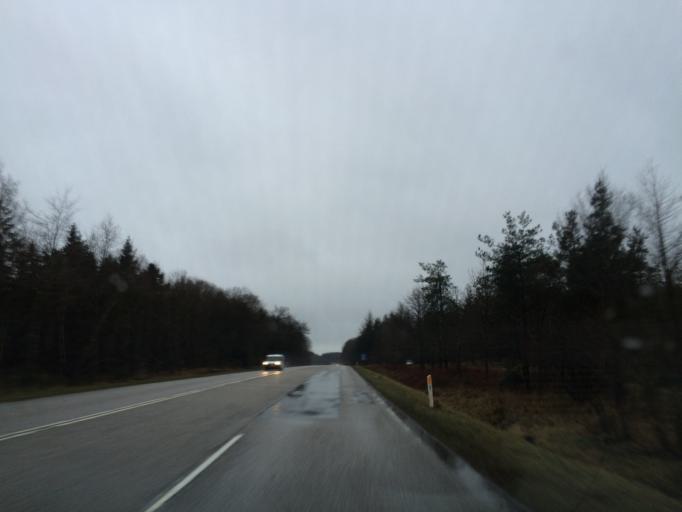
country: DK
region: North Denmark
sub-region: Mariagerfjord Kommune
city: Arden
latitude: 56.8164
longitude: 9.8198
